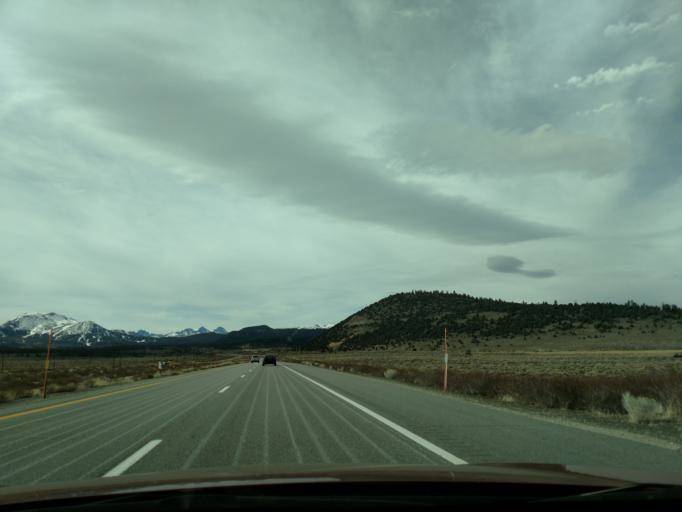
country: US
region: California
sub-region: Mono County
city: Mammoth Lakes
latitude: 37.6328
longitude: -118.8762
